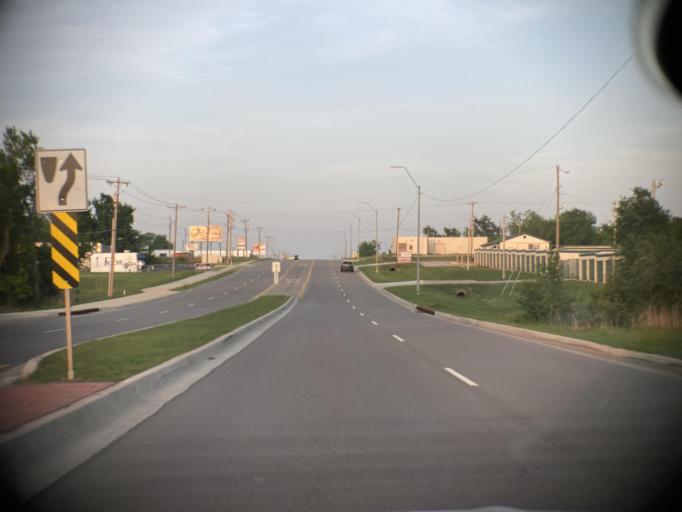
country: US
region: Oklahoma
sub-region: Oklahoma County
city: Midwest City
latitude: 35.4352
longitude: -97.3778
